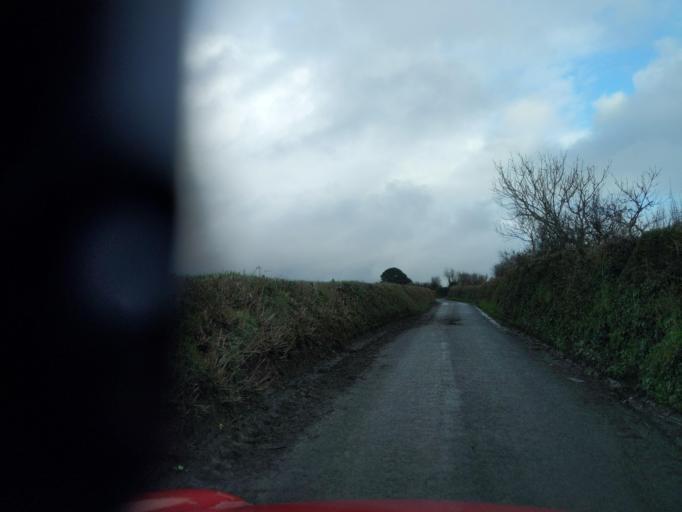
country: GB
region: England
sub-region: Devon
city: Yelverton
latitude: 50.4423
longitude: -4.1301
